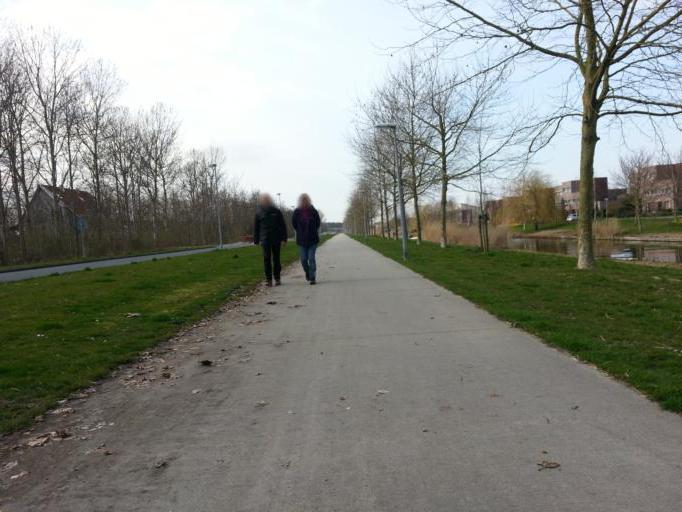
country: NL
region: Flevoland
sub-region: Gemeente Almere
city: Almere Stad
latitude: 52.3983
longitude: 5.3168
